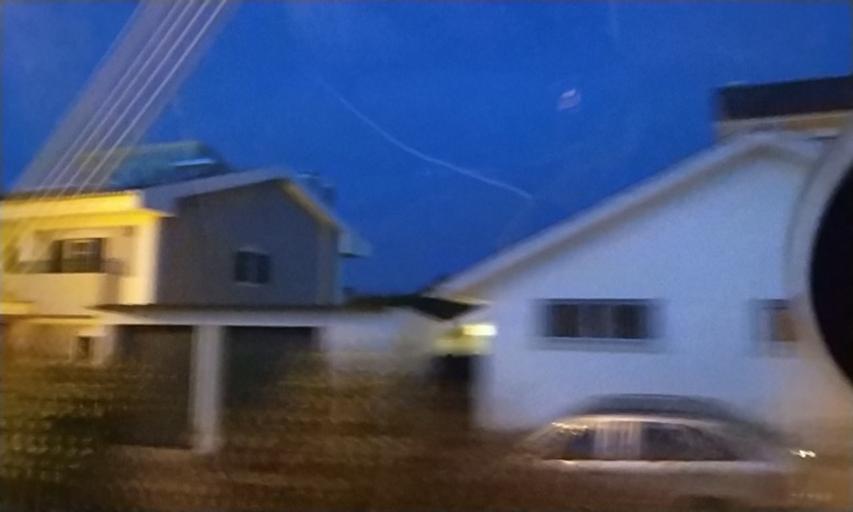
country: PT
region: Setubal
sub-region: Setubal
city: Setubal
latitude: 38.5374
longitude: -8.9017
